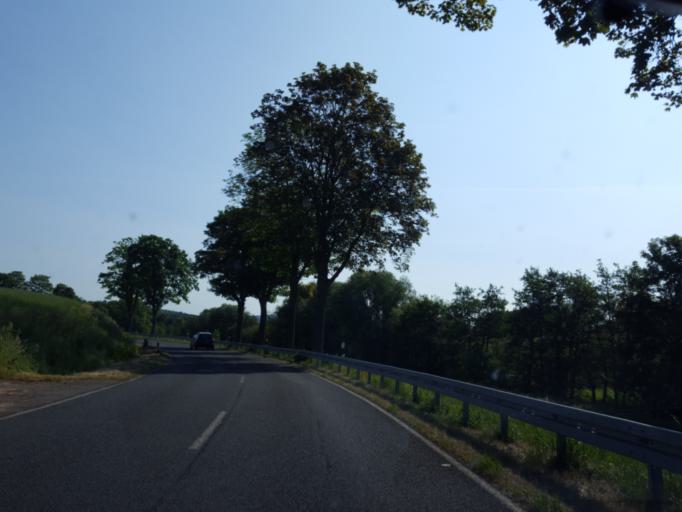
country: DE
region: Lower Saxony
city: Wulften
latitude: 51.6723
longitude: 10.2026
